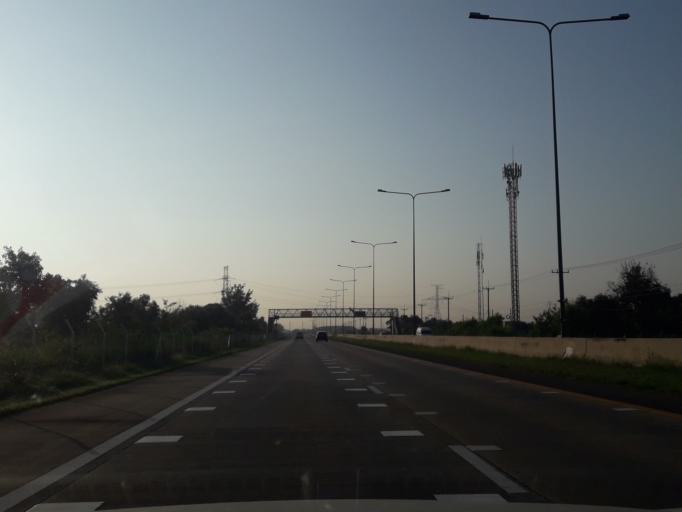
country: TH
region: Pathum Thani
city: Sam Khok
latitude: 14.1362
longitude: 100.5639
